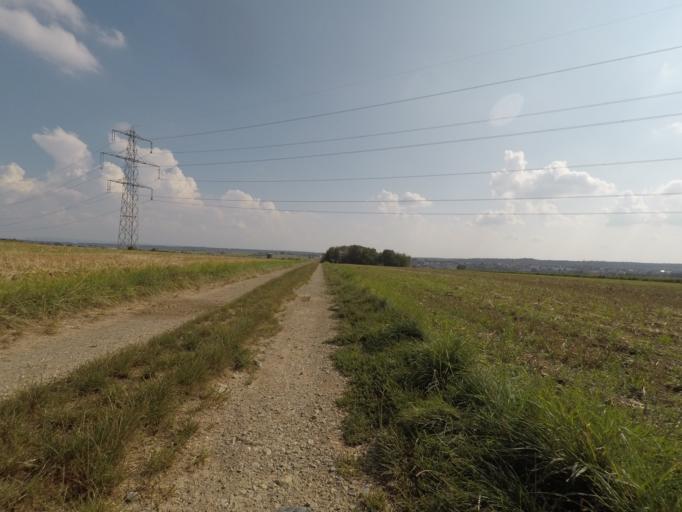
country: DE
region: Baden-Wuerttemberg
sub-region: Regierungsbezirk Stuttgart
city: Weil im Schonbuch
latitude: 48.6344
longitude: 9.0660
